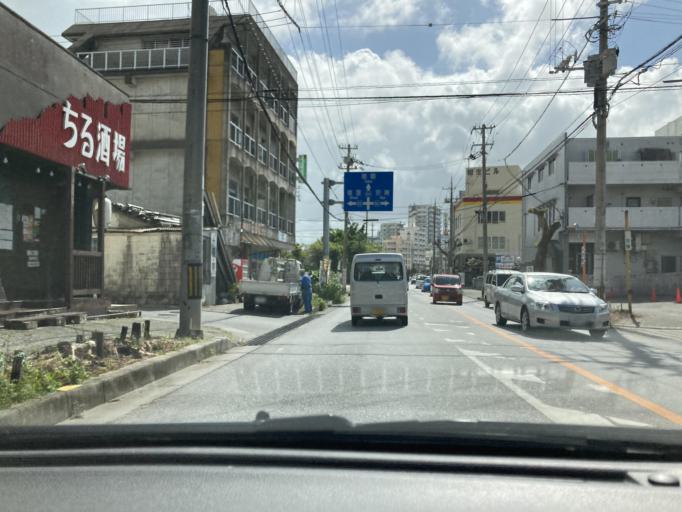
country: JP
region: Okinawa
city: Naha-shi
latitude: 26.2342
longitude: 127.7032
